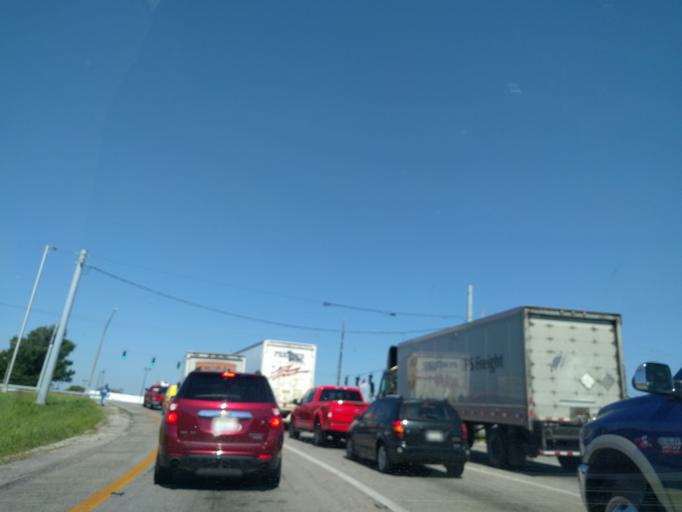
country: US
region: Kentucky
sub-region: Fayette County
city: Monticello
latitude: 37.9975
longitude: -84.5207
